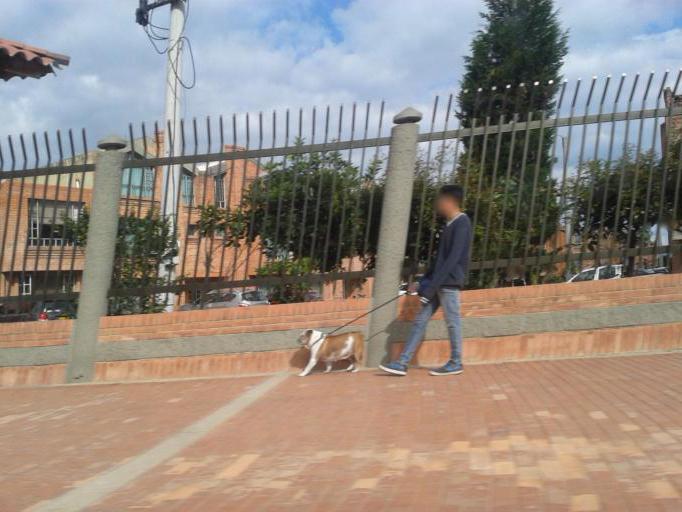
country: CO
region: Cundinamarca
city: Zipaquira
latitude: 5.0157
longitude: -74.0024
